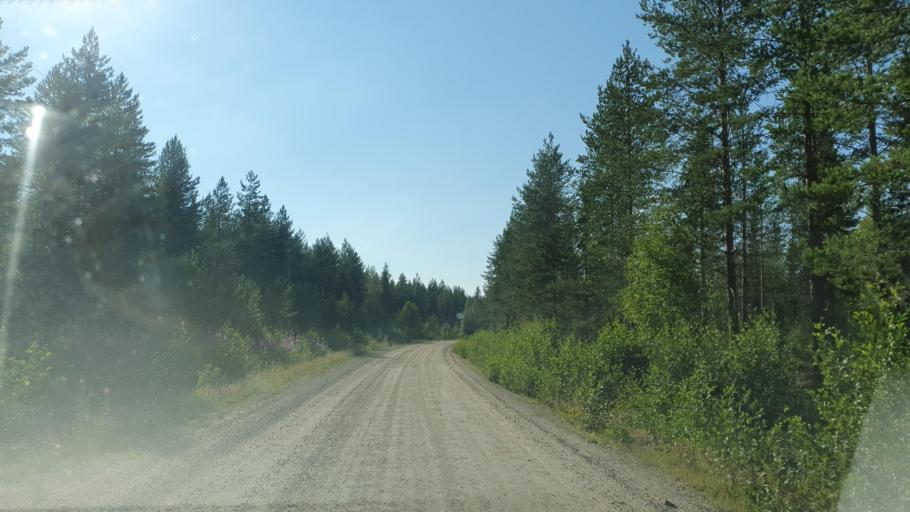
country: FI
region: Kainuu
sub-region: Kehys-Kainuu
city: Kuhmo
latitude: 64.0286
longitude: 29.7017
